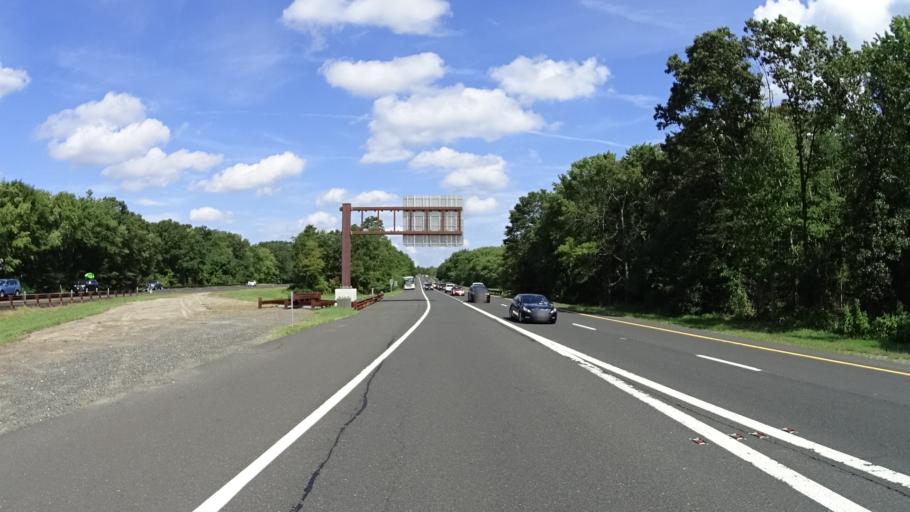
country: US
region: New Jersey
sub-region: Monmouth County
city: Strathmore
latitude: 40.4095
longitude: -74.2003
